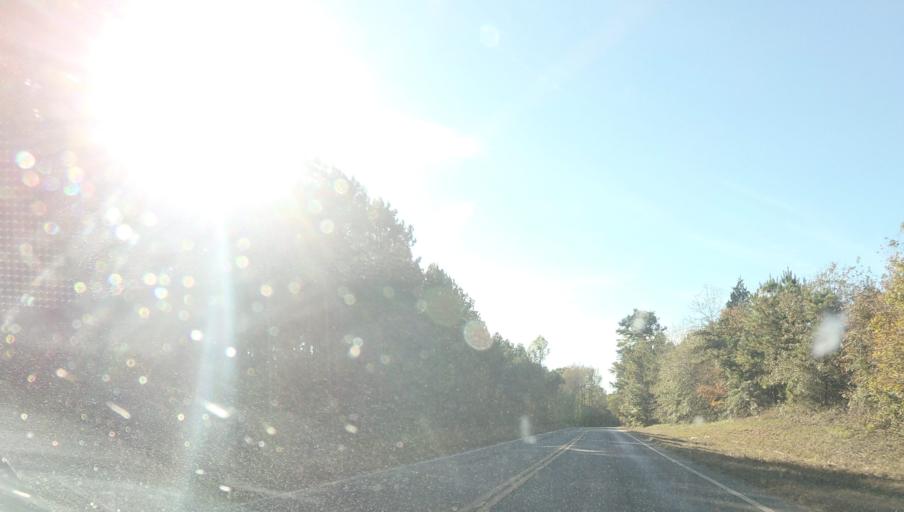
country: US
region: Georgia
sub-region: Talbot County
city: Talbotton
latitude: 32.6810
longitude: -84.5843
